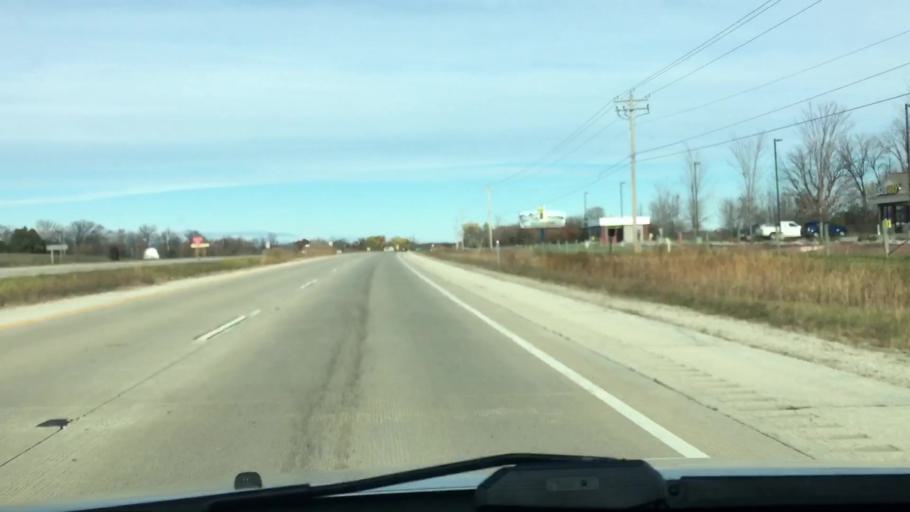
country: US
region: Wisconsin
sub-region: Brown County
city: Bellevue
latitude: 44.5753
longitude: -87.8749
